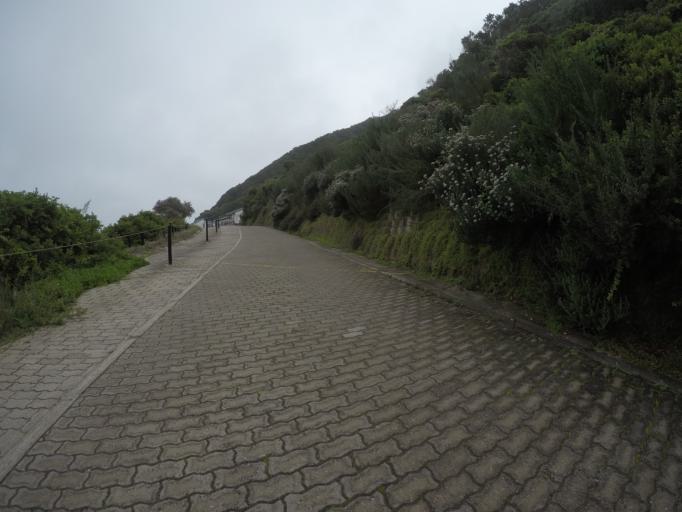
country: ZA
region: Eastern Cape
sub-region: Cacadu District Municipality
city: Kareedouw
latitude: -34.0715
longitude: 24.2221
